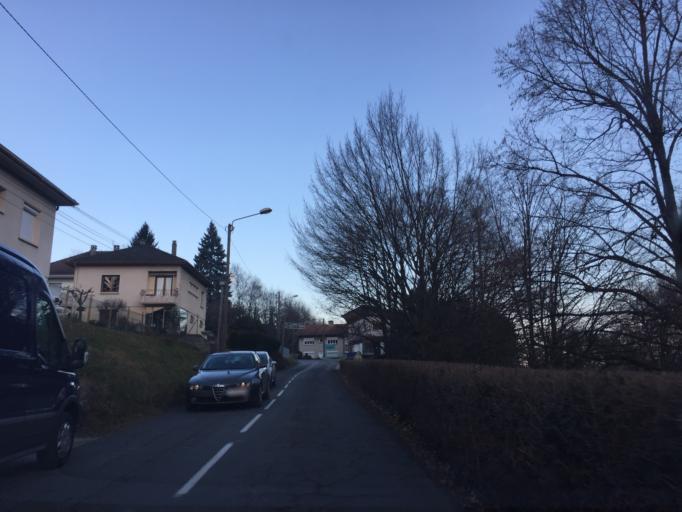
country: FR
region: Rhone-Alpes
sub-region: Departement de la Savoie
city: Tresserve
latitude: 45.6784
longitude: 5.9025
